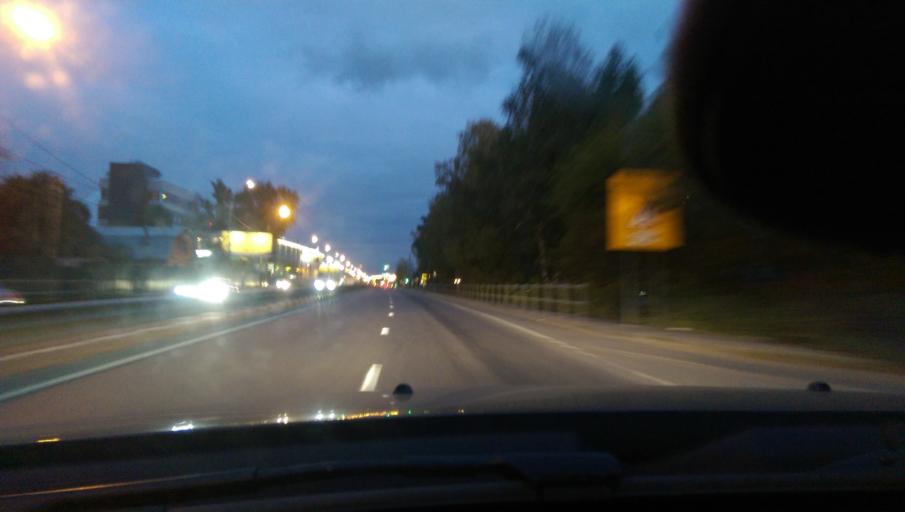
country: RU
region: Moscow
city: Vatutino
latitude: 55.9236
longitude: 37.6625
